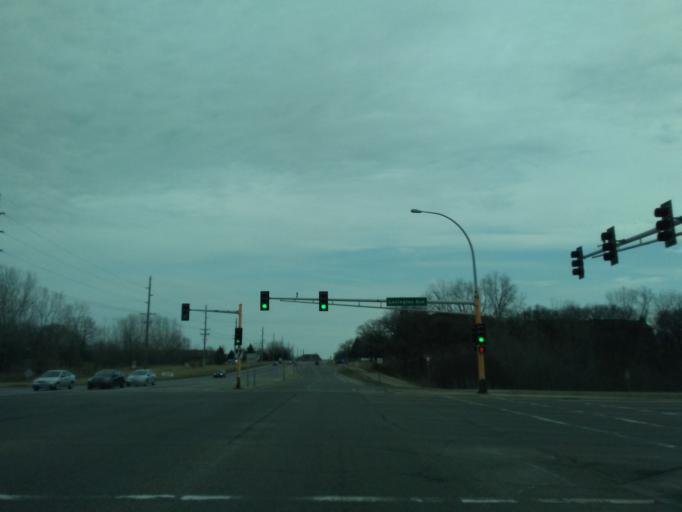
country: US
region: Minnesota
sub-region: Dakota County
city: Eagan
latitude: 44.8334
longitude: -93.1473
